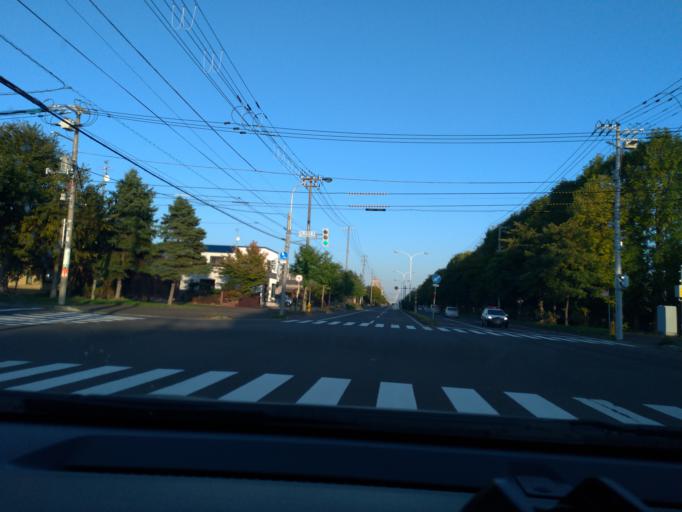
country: JP
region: Hokkaido
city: Ishikari
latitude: 43.1592
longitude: 141.3861
